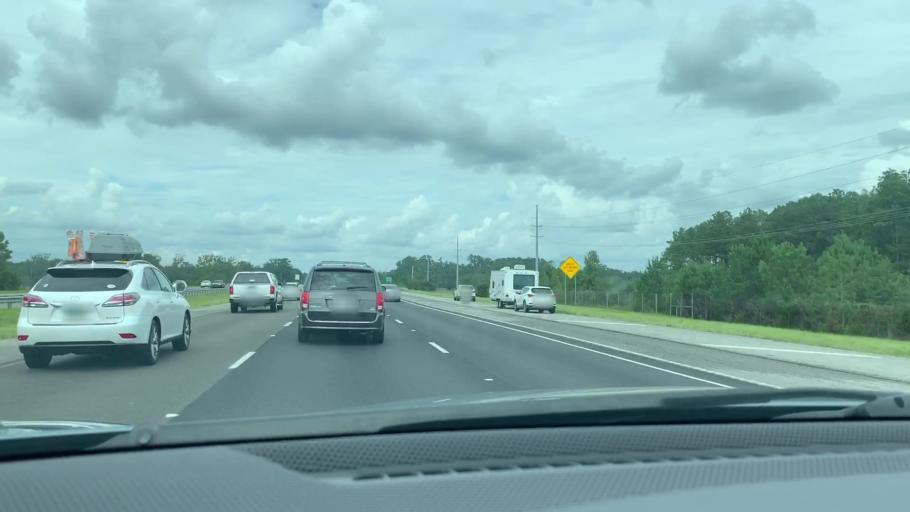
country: US
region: Georgia
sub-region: Liberty County
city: Midway
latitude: 31.8042
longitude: -81.3685
